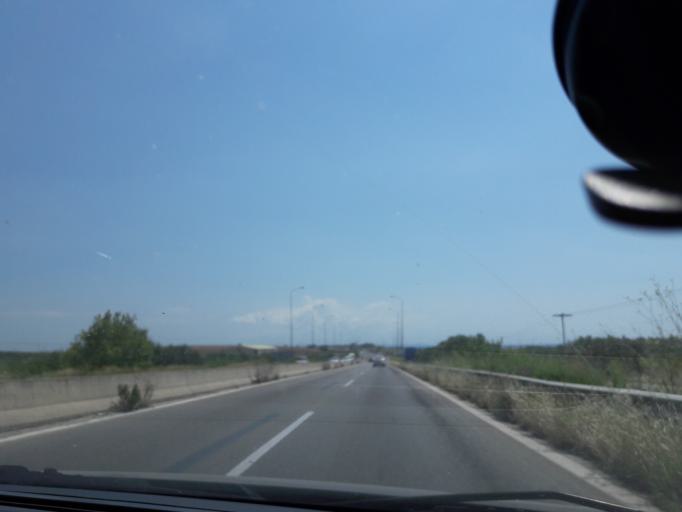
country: GR
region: Central Macedonia
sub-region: Nomos Chalkidikis
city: Nea Triglia
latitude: 40.2915
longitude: 23.1438
